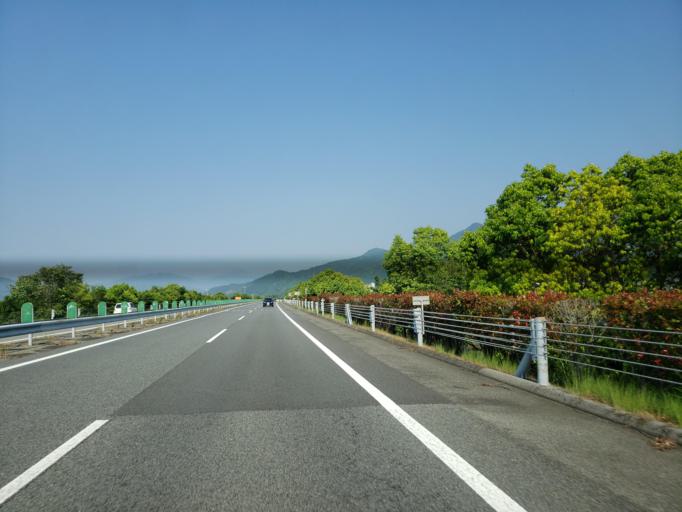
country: JP
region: Ehime
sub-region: Shikoku-chuo Shi
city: Matsuyama
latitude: 33.7864
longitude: 132.8629
